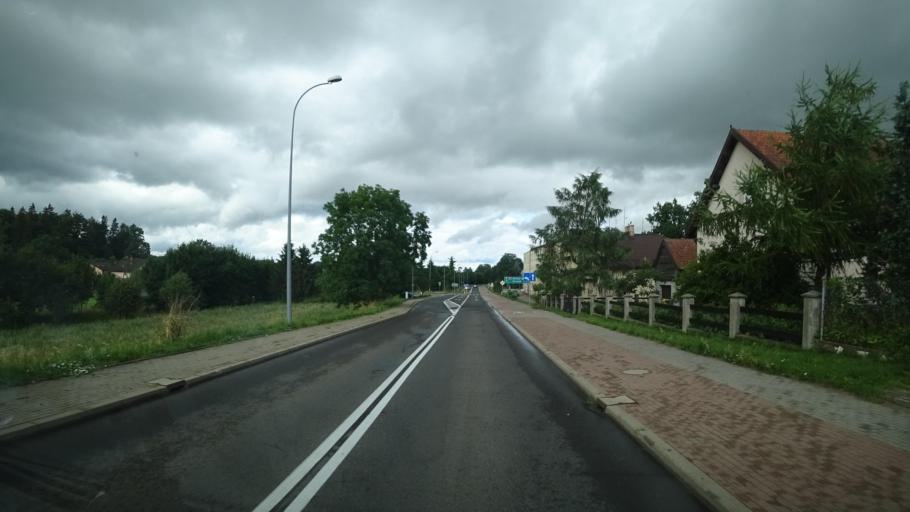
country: PL
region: Warmian-Masurian Voivodeship
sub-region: Powiat olecki
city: Kowale Oleckie
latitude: 54.1678
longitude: 22.4144
